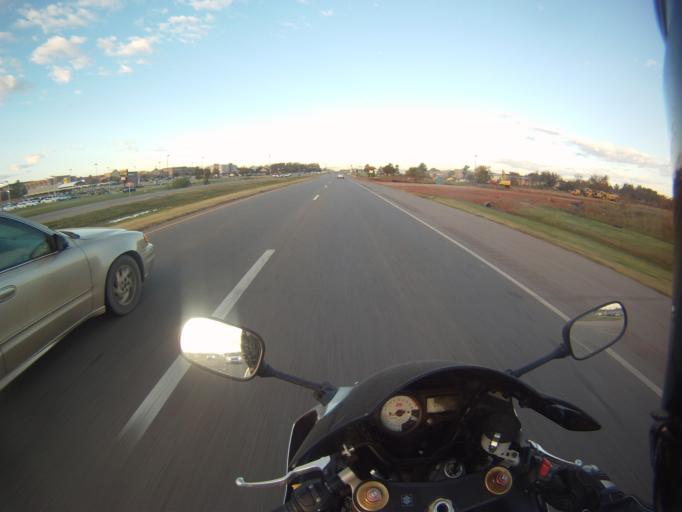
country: US
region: Oklahoma
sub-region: Payne County
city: Stillwater
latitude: 36.1161
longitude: -97.1165
